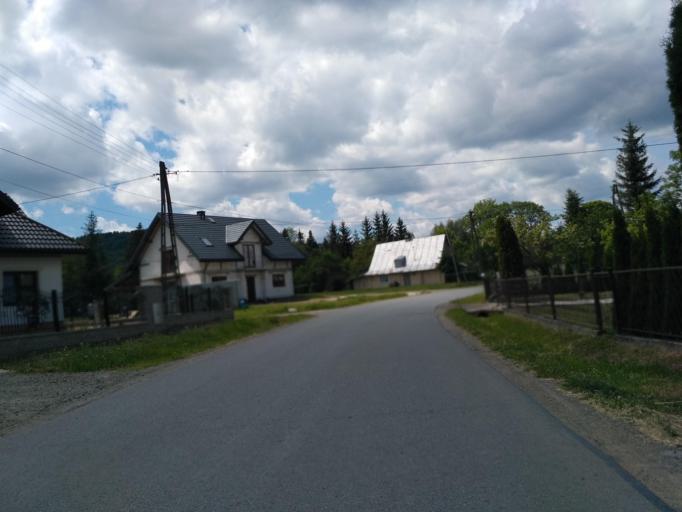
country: PL
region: Subcarpathian Voivodeship
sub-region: Powiat krosnienski
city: Dukla
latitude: 49.5541
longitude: 21.6694
